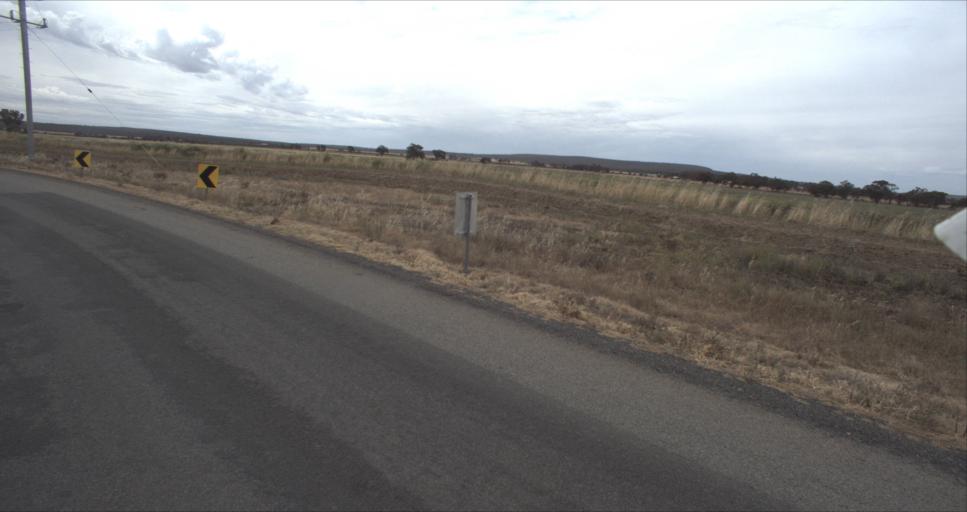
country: AU
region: New South Wales
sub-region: Leeton
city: Leeton
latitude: -34.4853
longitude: 146.4025
